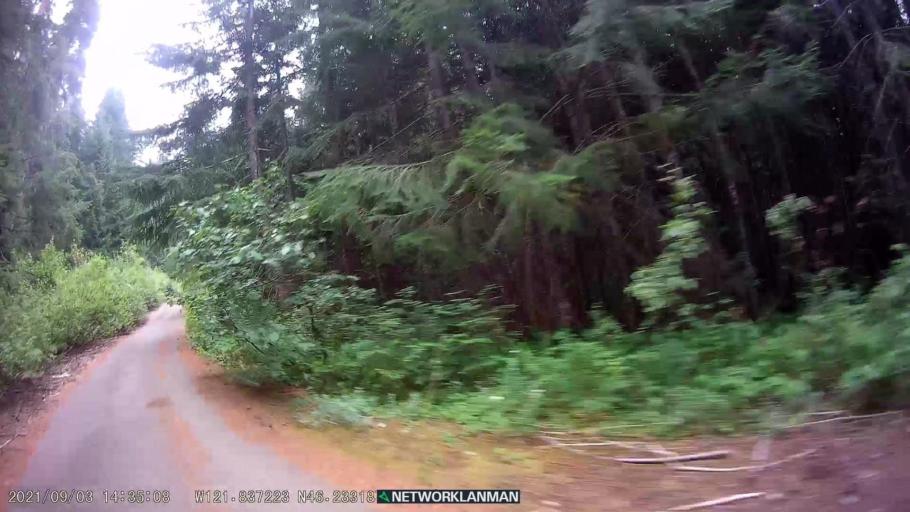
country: US
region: Washington
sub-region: Skamania County
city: Carson
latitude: 46.2330
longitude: -121.8369
